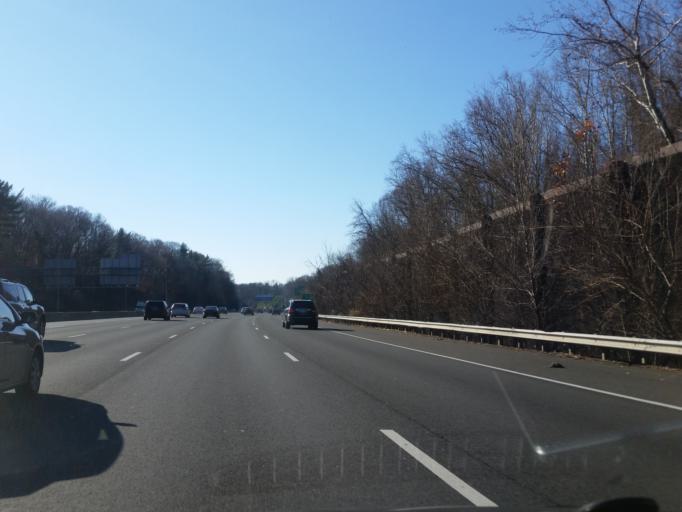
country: US
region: Maryland
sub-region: Montgomery County
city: Cabin John
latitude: 39.0058
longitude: -77.1540
